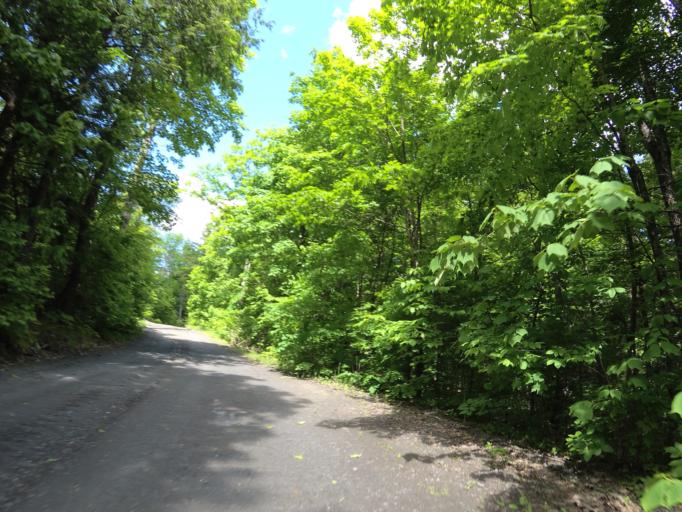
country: CA
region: Ontario
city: Renfrew
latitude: 45.0550
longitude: -76.8382
